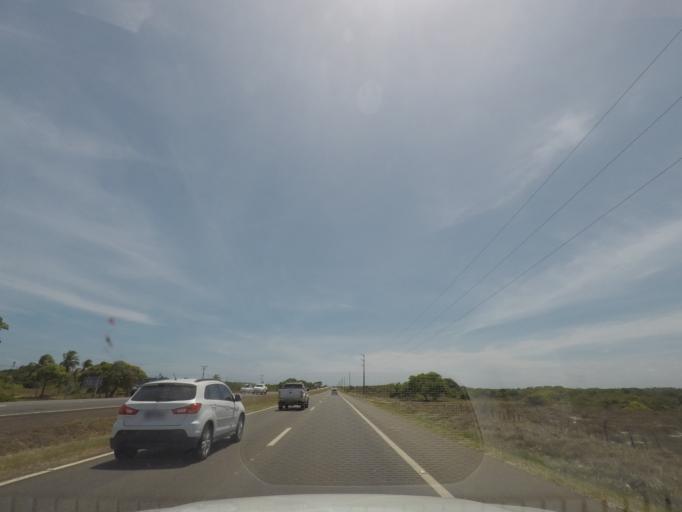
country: BR
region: Bahia
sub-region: Camacari
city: Camacari
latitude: -12.6665
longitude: -38.0952
